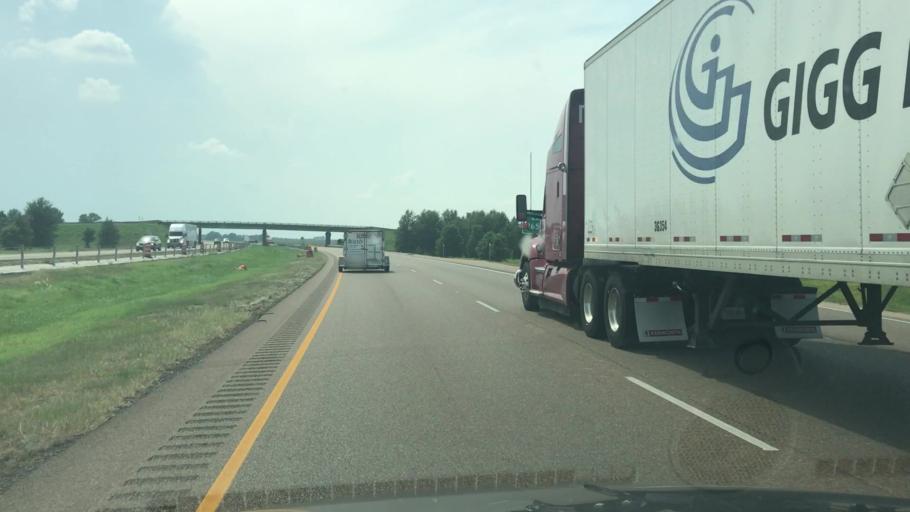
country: US
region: Arkansas
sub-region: Crittenden County
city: Earle
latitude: 35.1515
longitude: -90.3973
